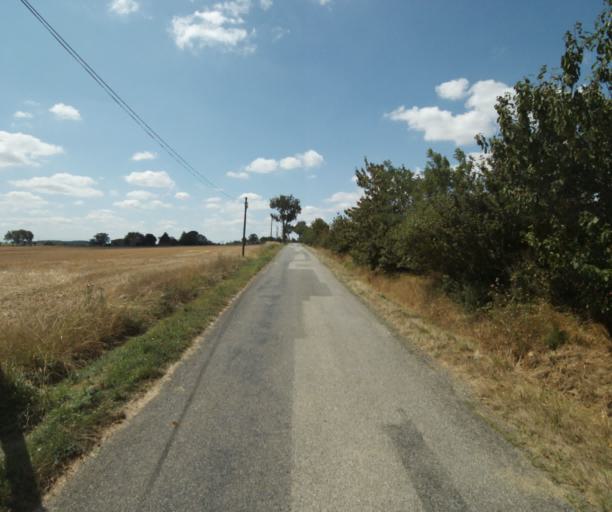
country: FR
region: Midi-Pyrenees
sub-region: Departement de la Haute-Garonne
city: Saint-Felix-Lauragais
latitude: 43.4650
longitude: 1.8421
